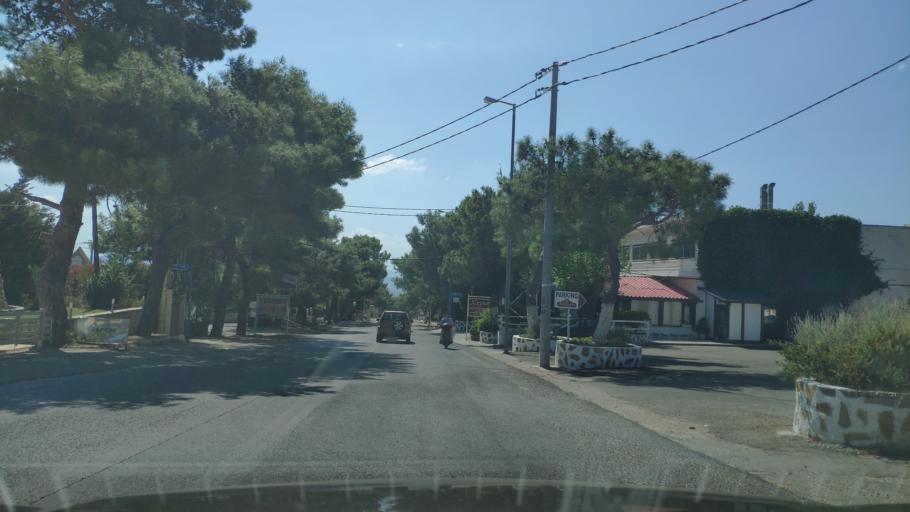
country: GR
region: Attica
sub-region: Nomarchia Anatolikis Attikis
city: Thrakomakedones
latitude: 38.1243
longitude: 23.7336
